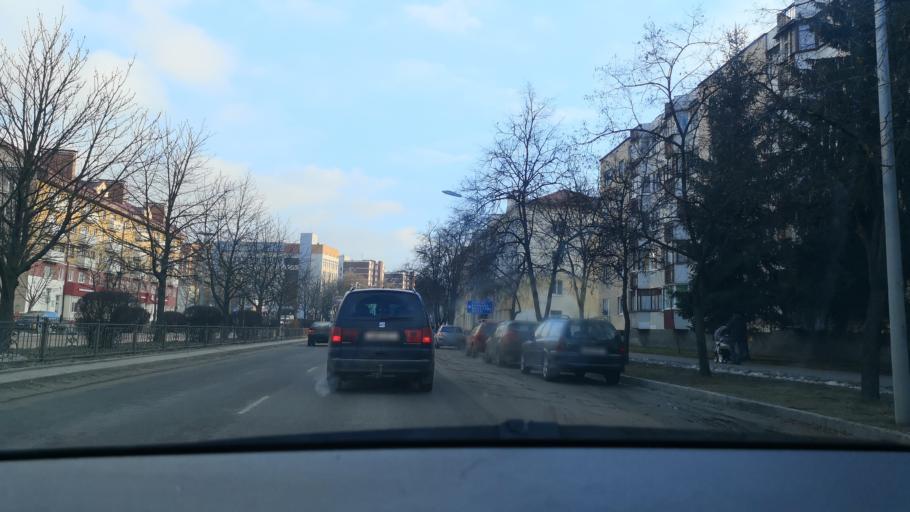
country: BY
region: Brest
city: Brest
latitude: 52.0953
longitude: 23.6982
